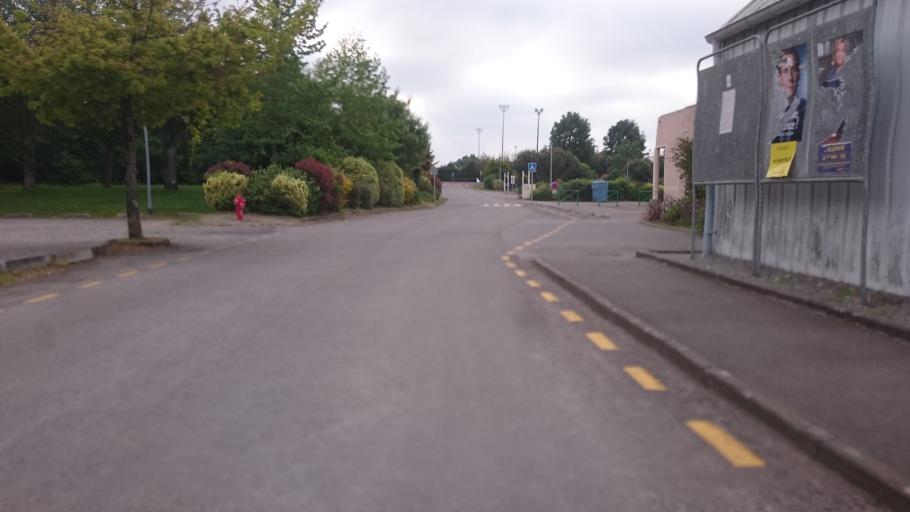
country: FR
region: Pays de la Loire
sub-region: Departement de la Loire-Atlantique
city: La Montagne
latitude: 47.1840
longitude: -1.6770
